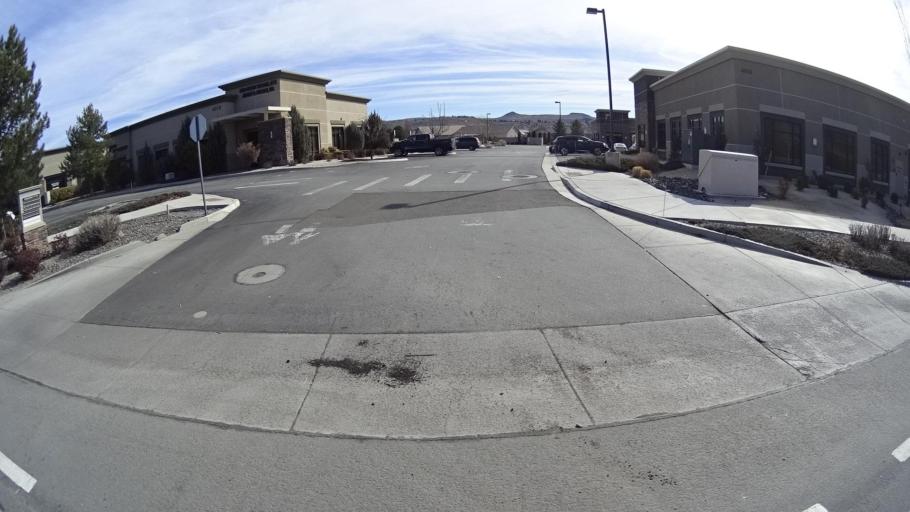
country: US
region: Nevada
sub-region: Washoe County
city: Sparks
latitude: 39.5793
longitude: -119.7241
